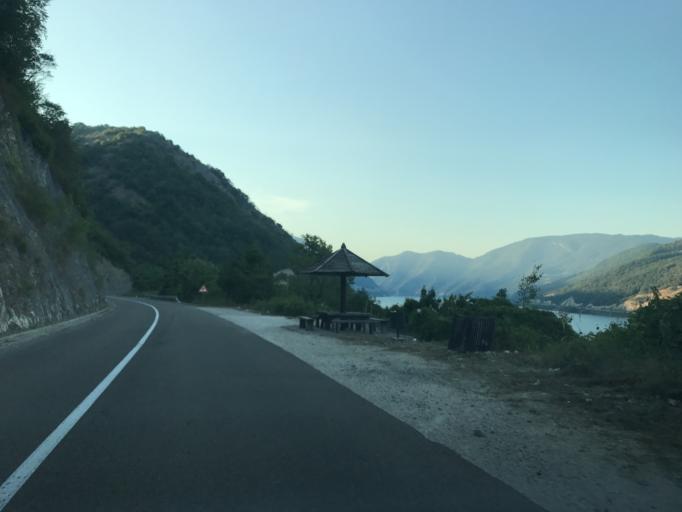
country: RO
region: Mehedinti
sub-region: Comuna Svinita
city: Svinita
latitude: 44.5500
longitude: 22.0281
